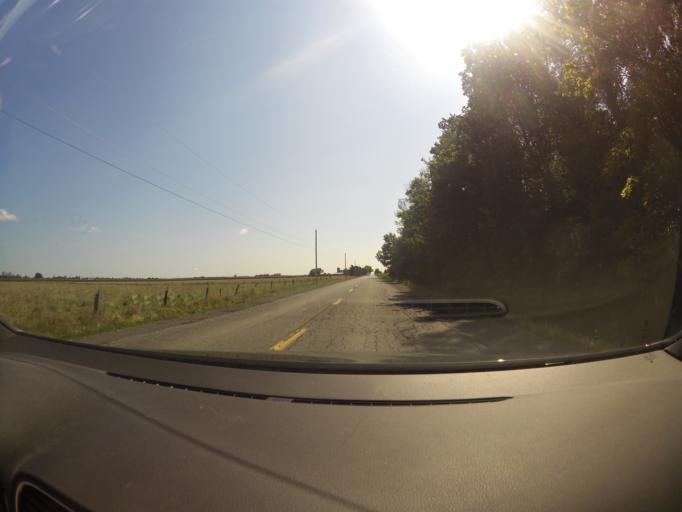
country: CA
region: Ontario
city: Arnprior
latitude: 45.3677
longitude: -76.2533
